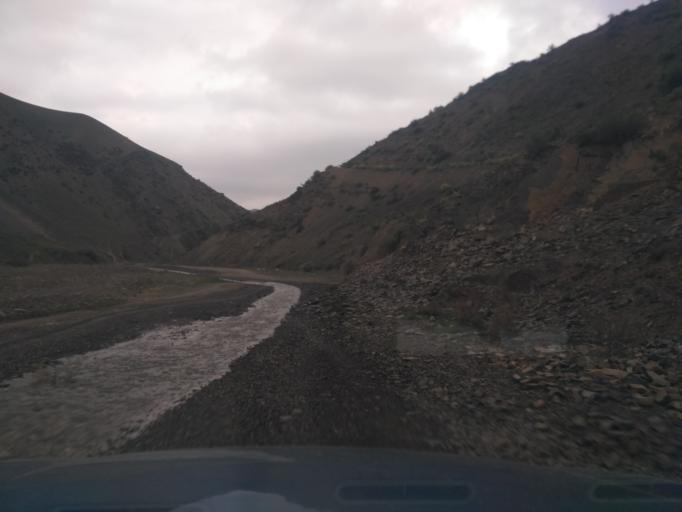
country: UZ
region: Jizzax
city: Zomin
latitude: 39.8587
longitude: 68.3874
